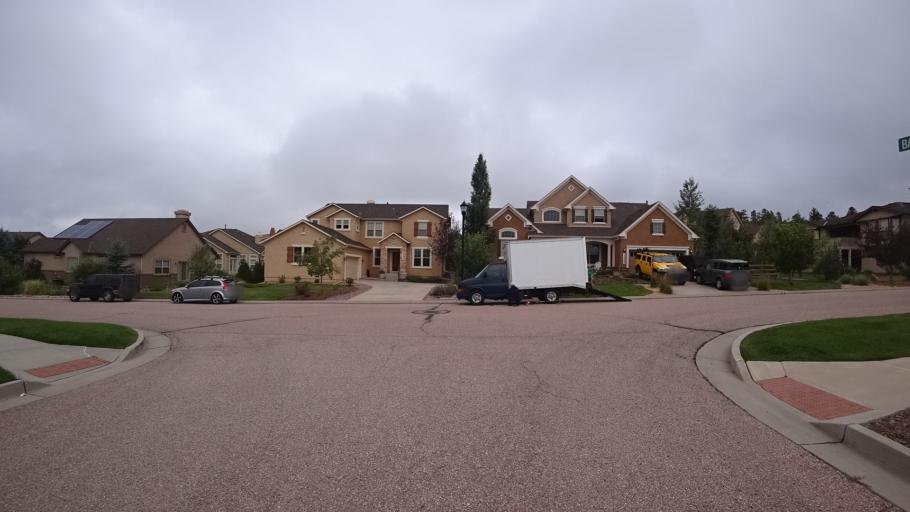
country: US
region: Colorado
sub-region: El Paso County
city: Gleneagle
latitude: 39.0333
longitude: -104.7810
